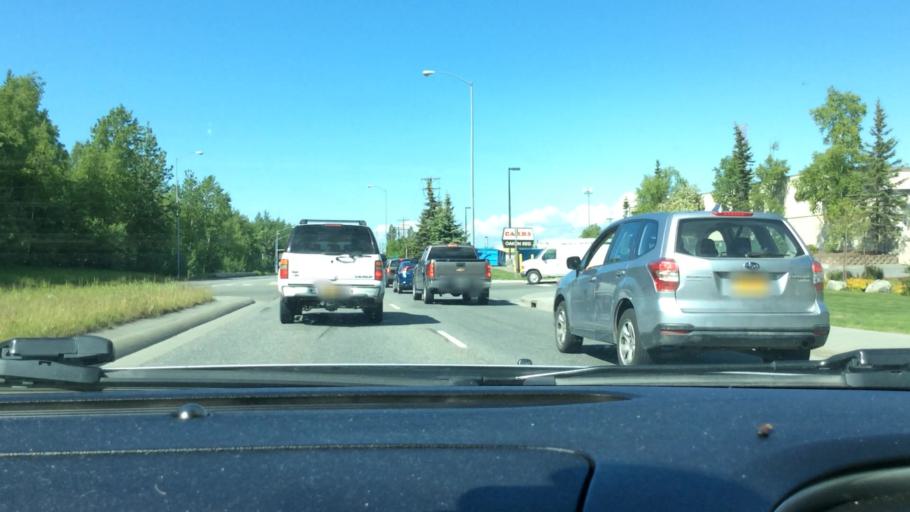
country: US
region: Alaska
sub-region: Anchorage Municipality
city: Anchorage
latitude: 61.2073
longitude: -149.7783
